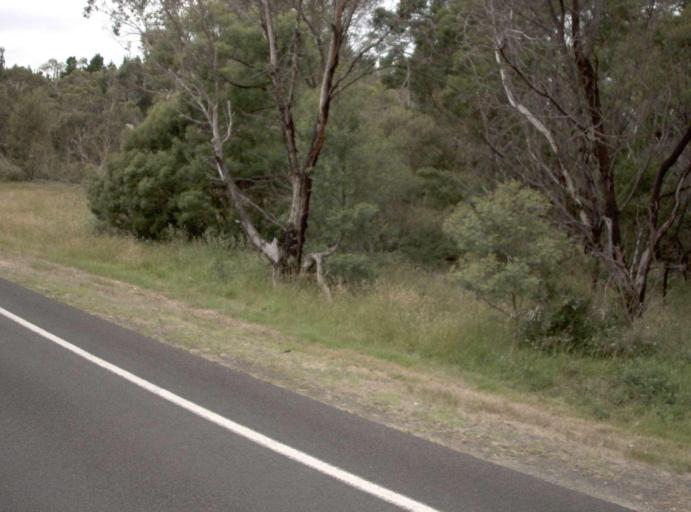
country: AU
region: Victoria
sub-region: Wellington
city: Sale
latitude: -38.2171
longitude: 147.0606
